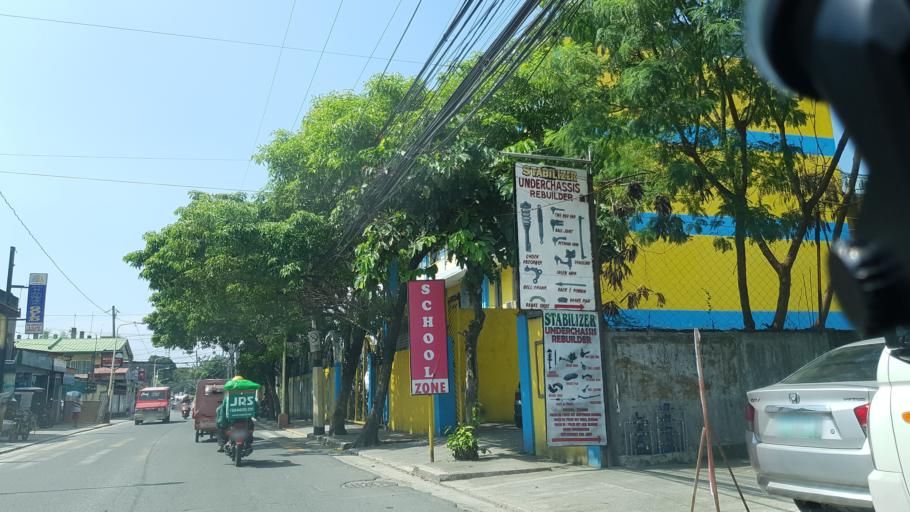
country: PH
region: Calabarzon
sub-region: Province of Rizal
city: Las Pinas
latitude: 14.4666
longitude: 120.9828
